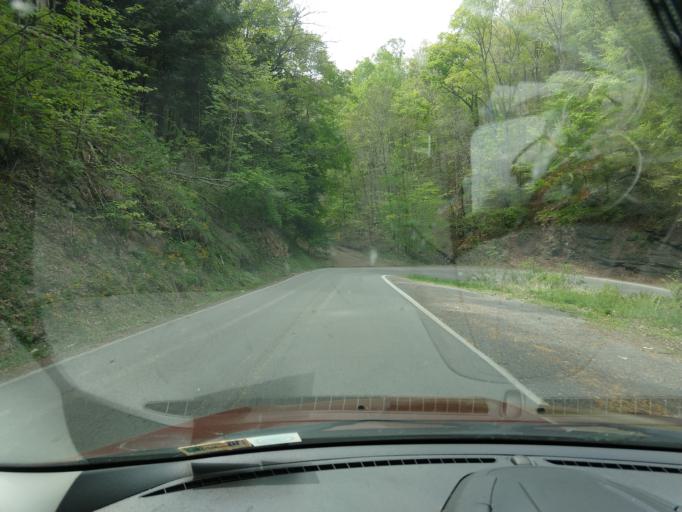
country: US
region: West Virginia
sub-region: McDowell County
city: Welch
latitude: 37.3657
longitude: -81.6422
